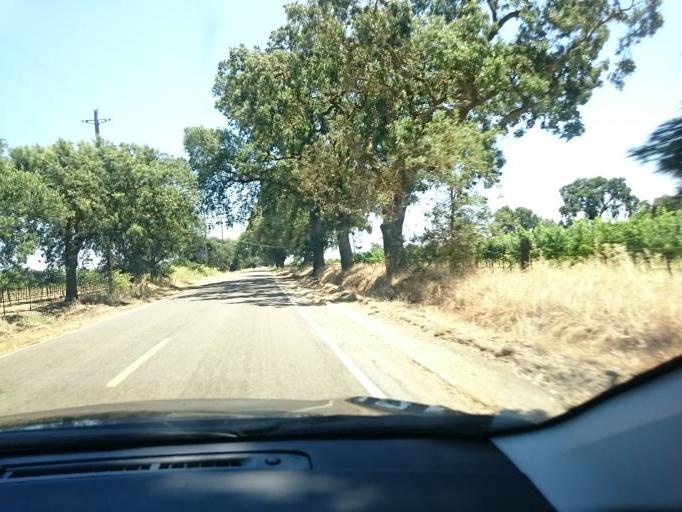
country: US
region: California
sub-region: San Joaquin County
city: Thornton
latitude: 38.2039
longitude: -121.3967
